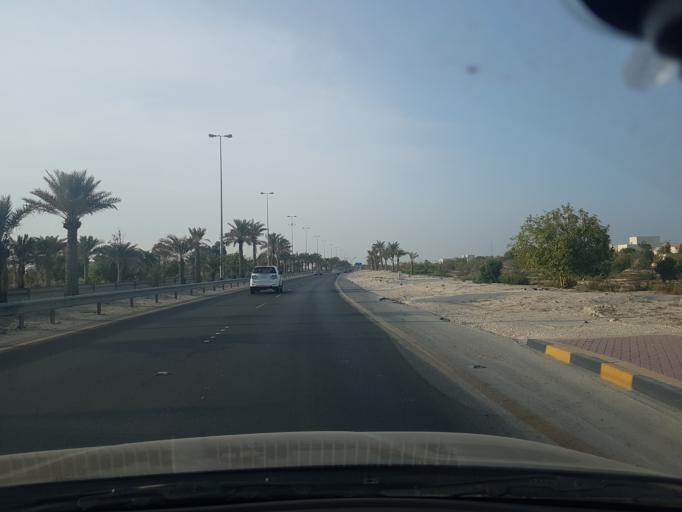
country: BH
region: Northern
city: Ar Rifa'
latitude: 26.1360
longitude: 50.5383
